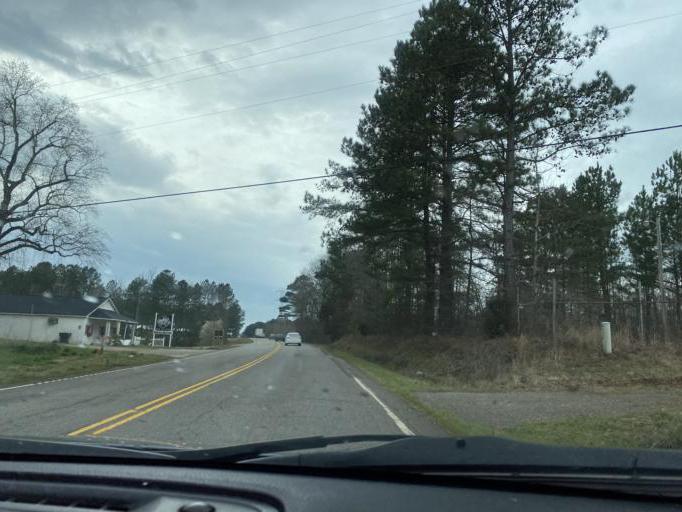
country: US
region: South Carolina
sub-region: Spartanburg County
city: Cowpens
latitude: 35.0158
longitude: -81.7530
